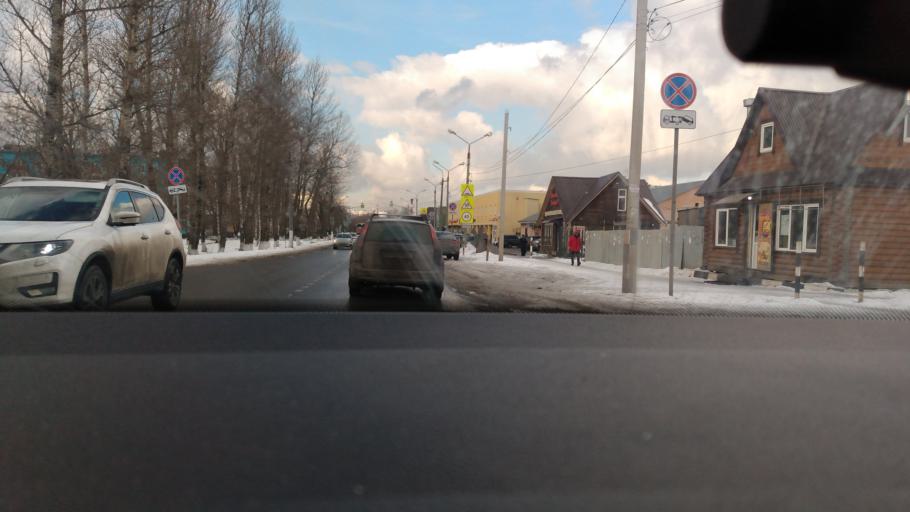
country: RU
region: Moskovskaya
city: Zheleznodorozhnyy
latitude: 55.7231
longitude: 38.0411
